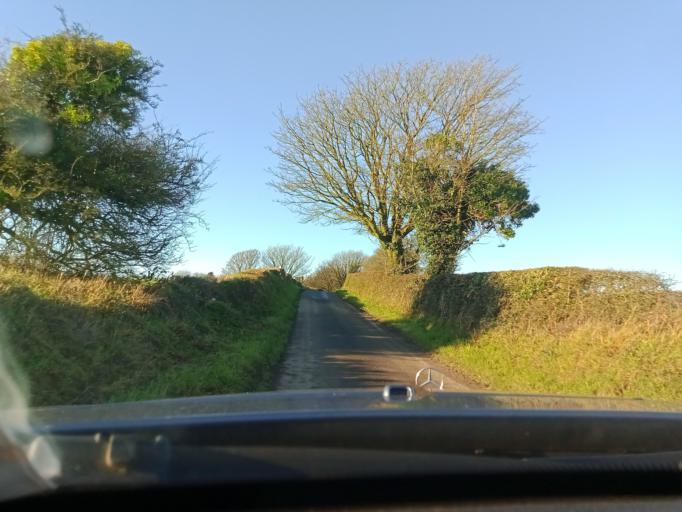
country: IE
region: Leinster
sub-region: Kilkenny
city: Callan
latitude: 52.4606
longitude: -7.4094
